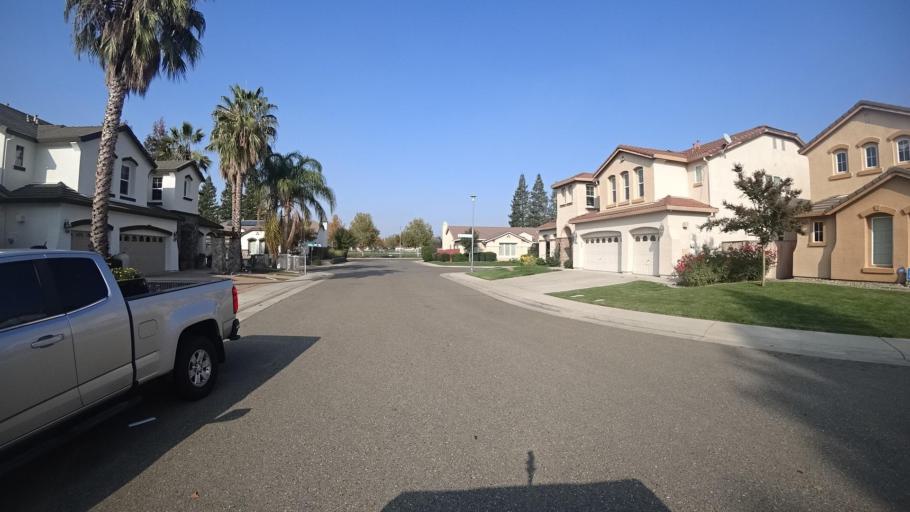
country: US
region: California
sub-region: Sacramento County
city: Elk Grove
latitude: 38.4227
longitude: -121.3368
